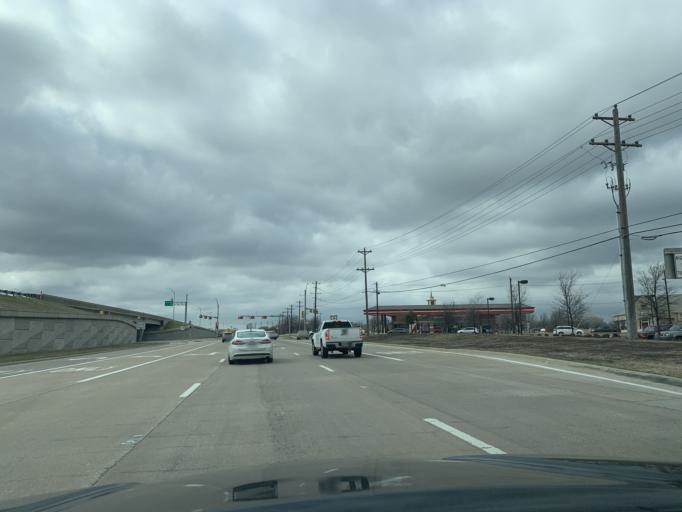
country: US
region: Texas
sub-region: Collin County
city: Frisco
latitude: 33.1201
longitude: -96.7495
